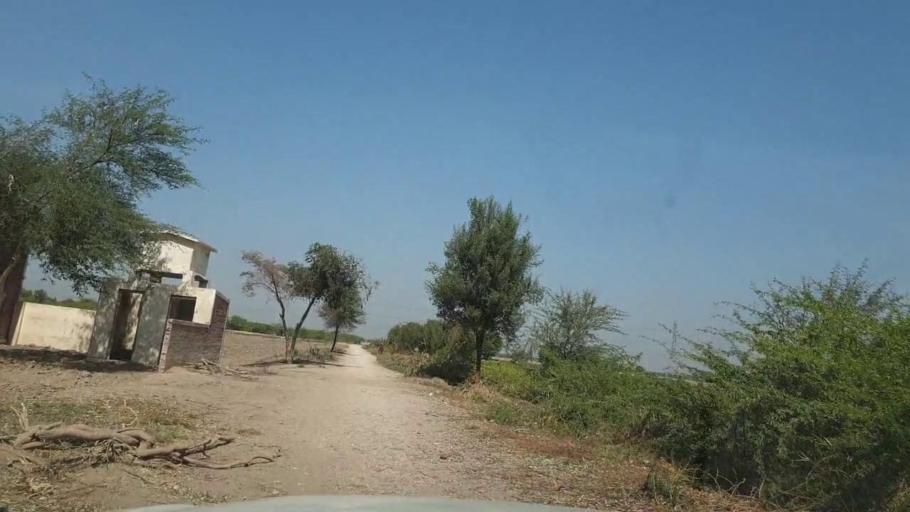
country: PK
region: Sindh
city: Kunri
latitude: 25.0978
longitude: 69.4583
